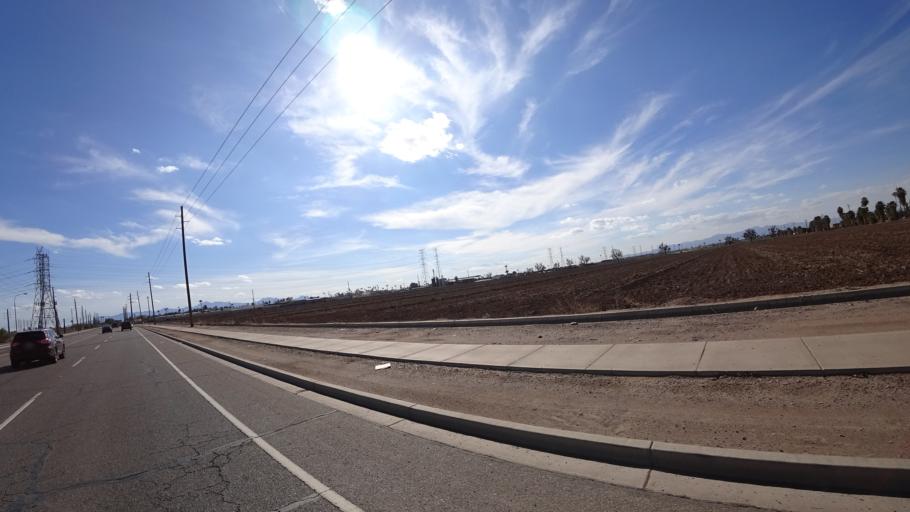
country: US
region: Arizona
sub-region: Maricopa County
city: Peoria
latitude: 33.5589
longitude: -112.2205
